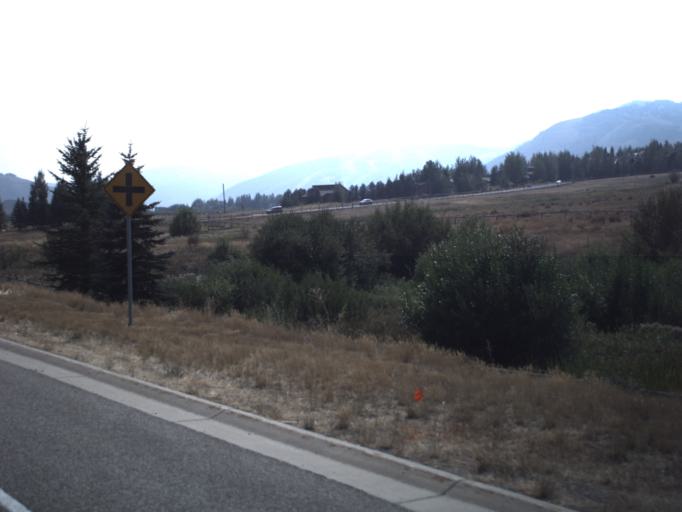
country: US
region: Utah
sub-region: Summit County
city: Snyderville
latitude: 40.6765
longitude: -111.5225
